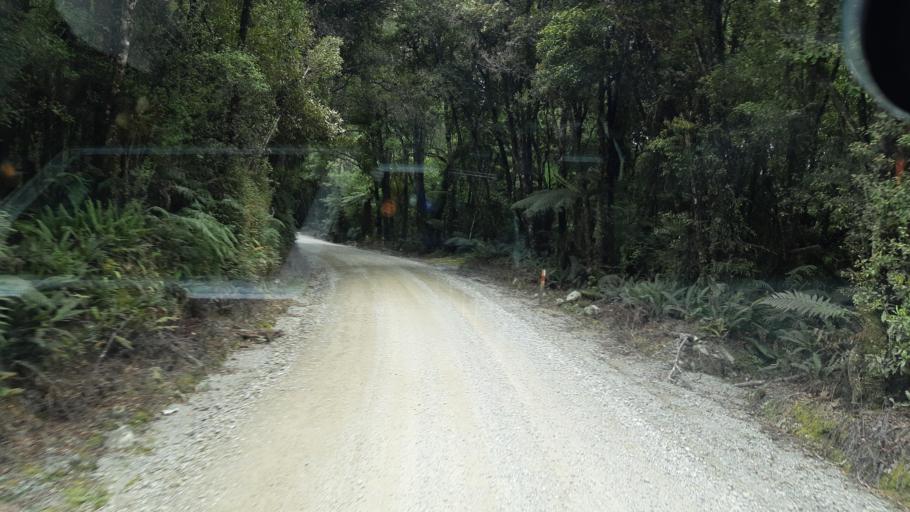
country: NZ
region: West Coast
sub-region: Grey District
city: Greymouth
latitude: -42.7263
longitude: 171.2358
